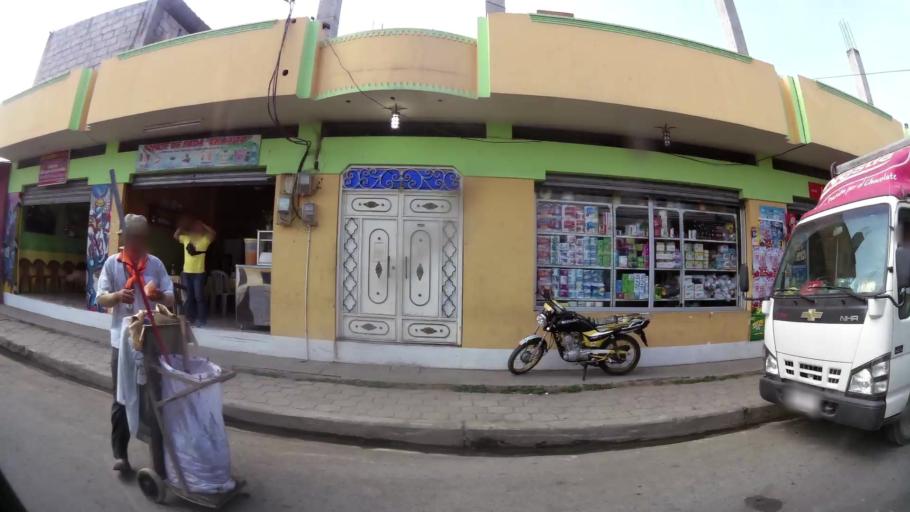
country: EC
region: Guayas
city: Eloy Alfaro
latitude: -2.1740
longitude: -79.8293
